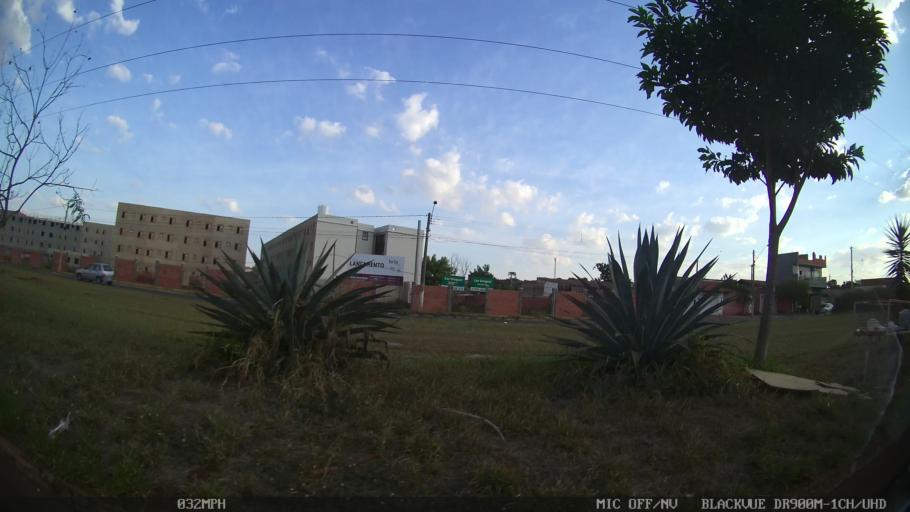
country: BR
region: Sao Paulo
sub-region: Ribeirao Preto
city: Ribeirao Preto
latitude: -21.1947
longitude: -47.7350
